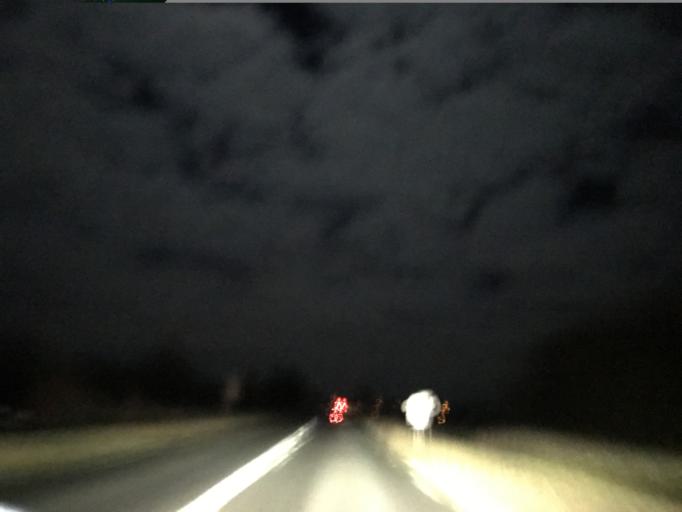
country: FR
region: Auvergne
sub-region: Departement de l'Allier
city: Hauterive
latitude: 46.0879
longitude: 3.4424
